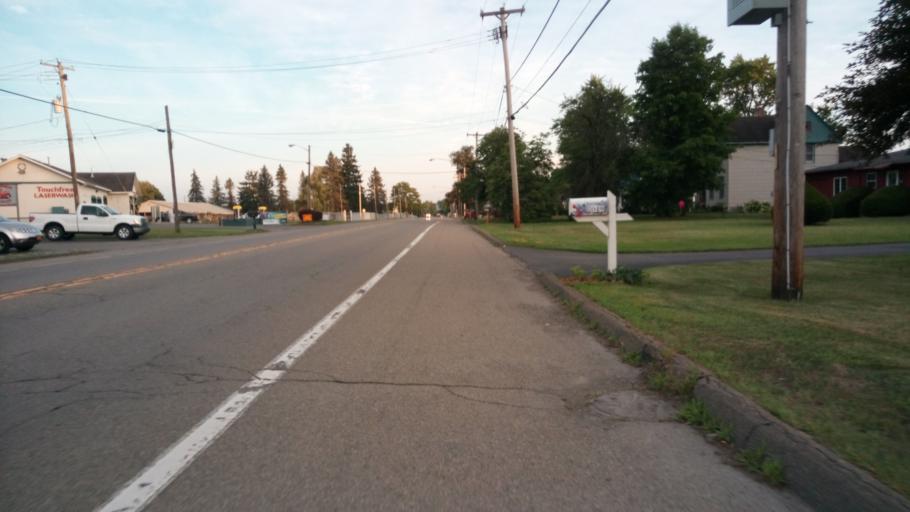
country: US
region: New York
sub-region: Chemung County
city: Horseheads
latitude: 42.1493
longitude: -76.8211
